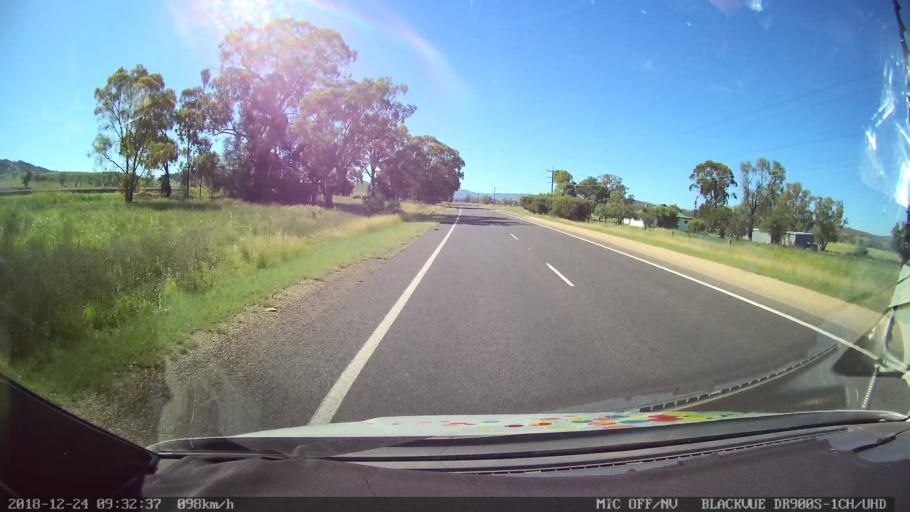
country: AU
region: New South Wales
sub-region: Liverpool Plains
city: Quirindi
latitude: -31.5930
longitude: 150.7033
